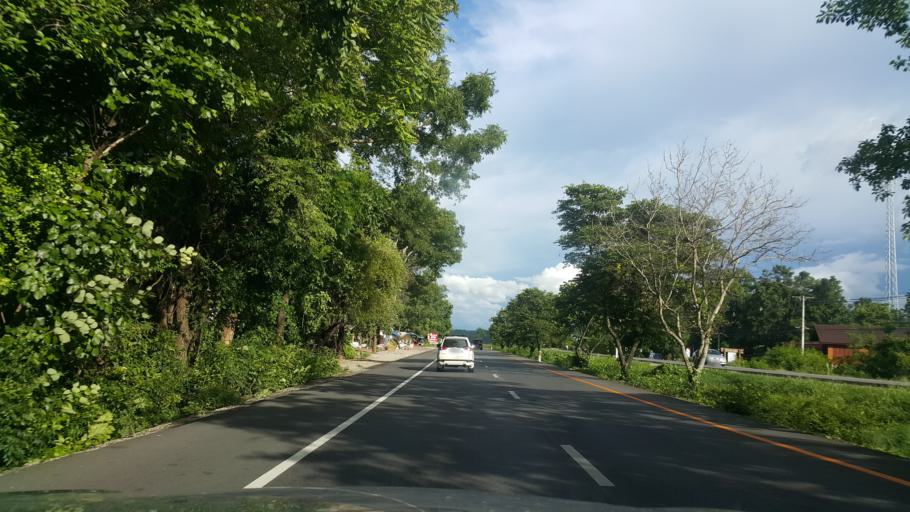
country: TH
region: Tak
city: Ban Tak
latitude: 17.0208
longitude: 99.0991
